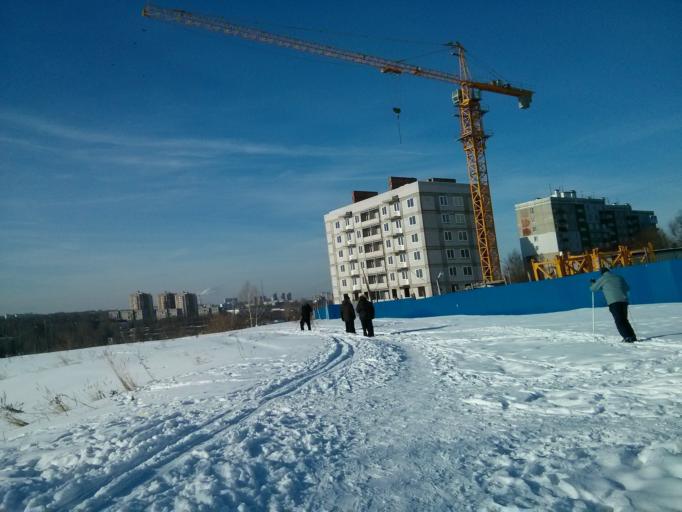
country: RU
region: Nizjnij Novgorod
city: Afonino
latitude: 56.2922
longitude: 44.0617
